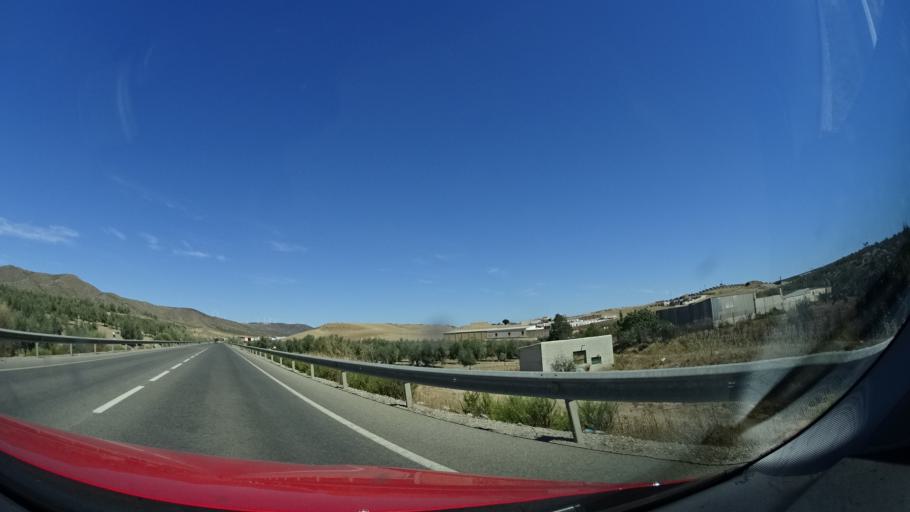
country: ES
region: Andalusia
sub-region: Provincia de Malaga
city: Sierra de Yeguas
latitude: 37.1195
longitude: -4.8788
